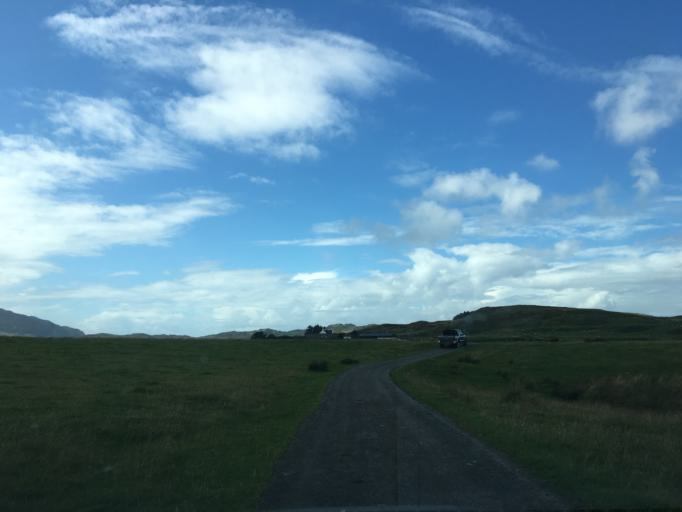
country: GB
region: Scotland
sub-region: Argyll and Bute
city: Oban
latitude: 56.2205
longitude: -5.6449
